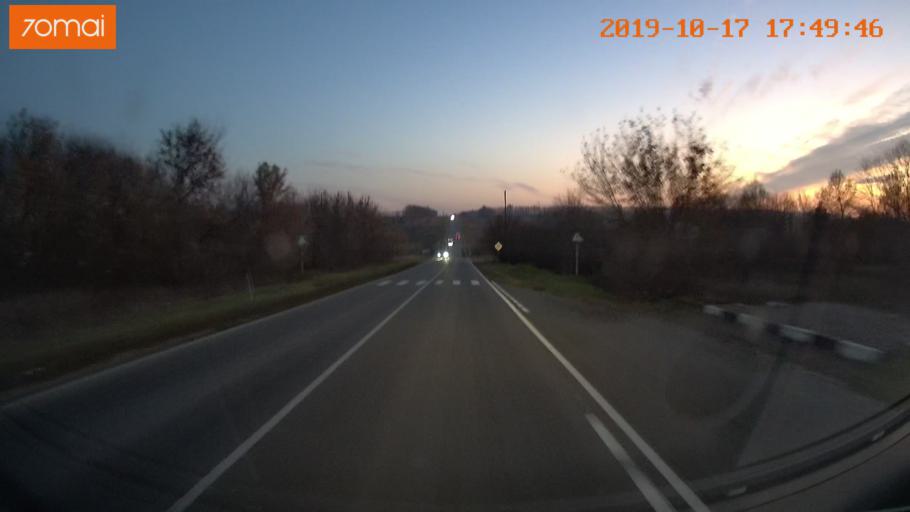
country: RU
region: Tula
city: Yepifan'
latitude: 53.6723
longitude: 38.6895
